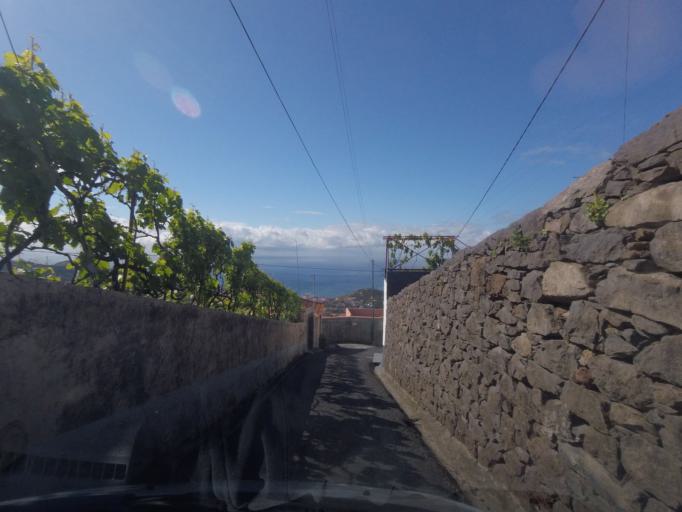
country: PT
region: Madeira
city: Camara de Lobos
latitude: 32.6674
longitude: -16.9759
